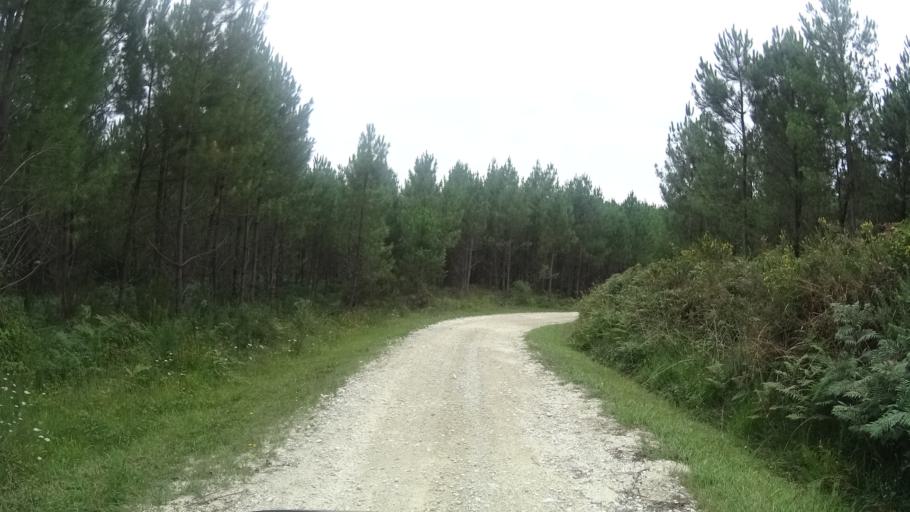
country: FR
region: Aquitaine
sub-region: Departement de la Dordogne
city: Neuvic
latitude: 45.0300
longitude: 0.5338
